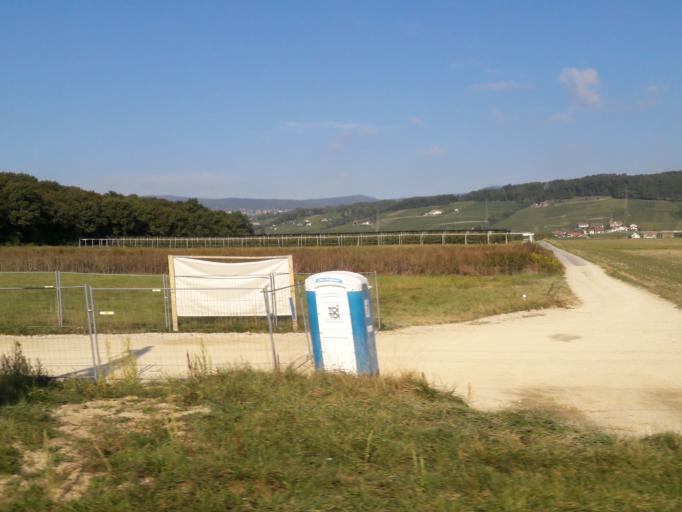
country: CH
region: Vaud
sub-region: Nyon District
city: Gland
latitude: 46.4320
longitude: 6.2815
